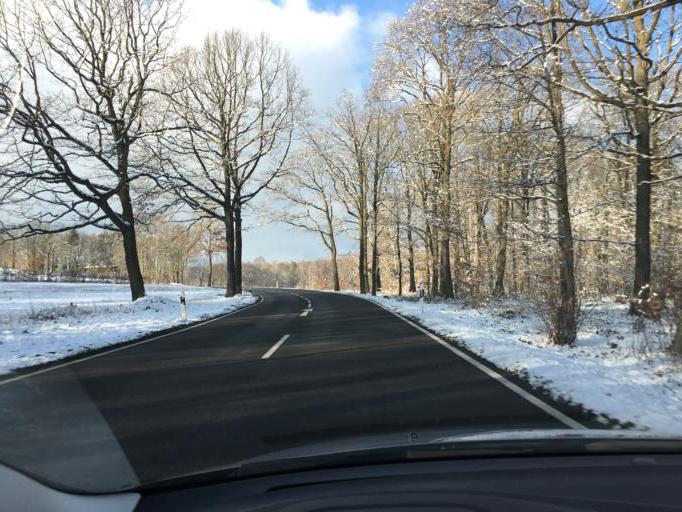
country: DE
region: Saxony
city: Grimma
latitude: 51.2706
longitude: 12.6666
